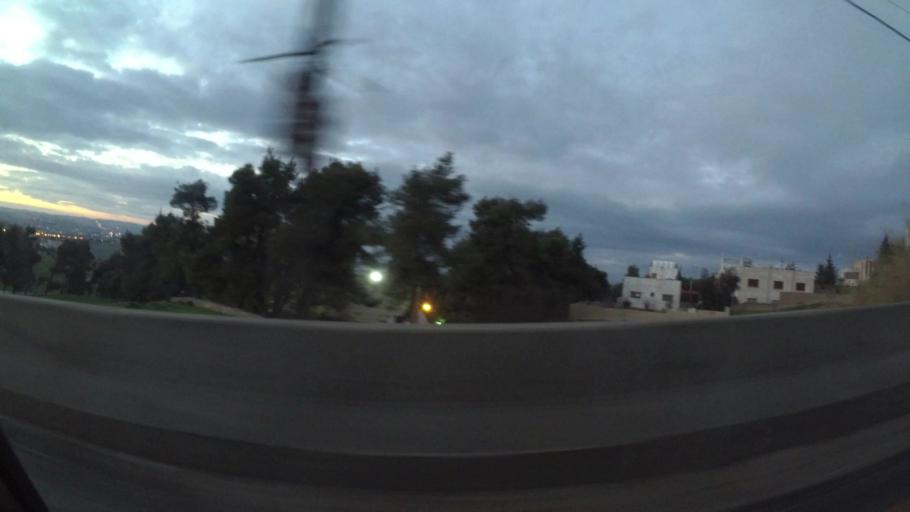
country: JO
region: Amman
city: Al Jubayhah
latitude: 32.0290
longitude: 35.8066
